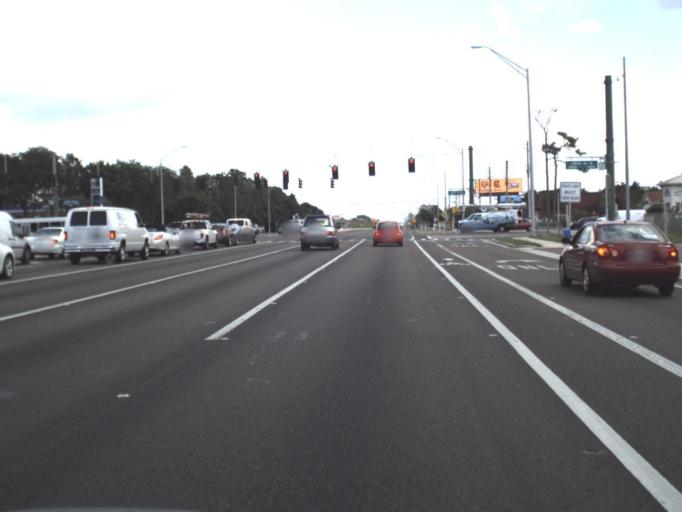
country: US
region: Florida
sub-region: Pinellas County
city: South Highpoint
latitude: 27.8938
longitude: -82.7014
